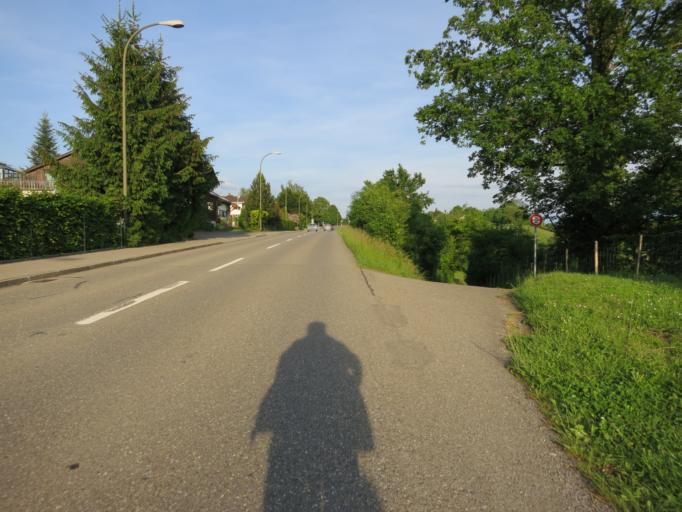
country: CH
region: Zurich
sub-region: Bezirk Hinwil
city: Gossau
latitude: 47.3004
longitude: 8.7645
